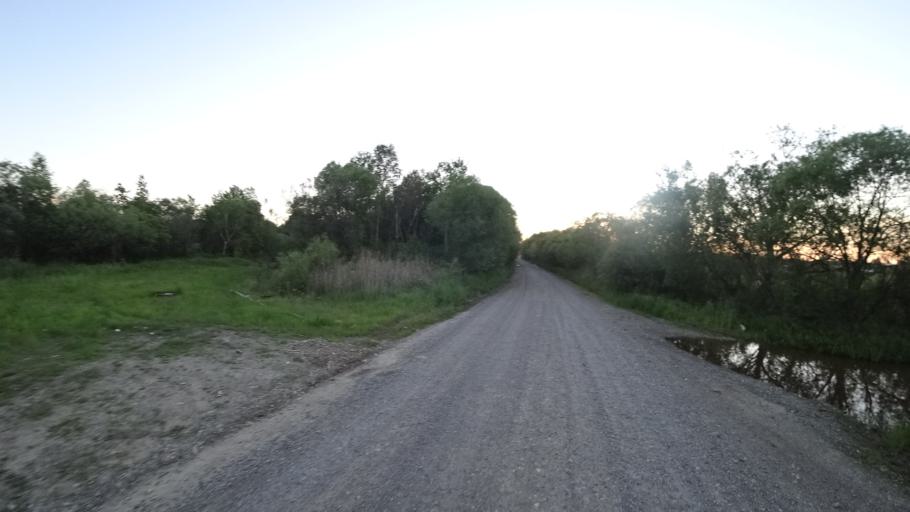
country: RU
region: Khabarovsk Krai
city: Khor
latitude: 47.8422
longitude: 134.9554
